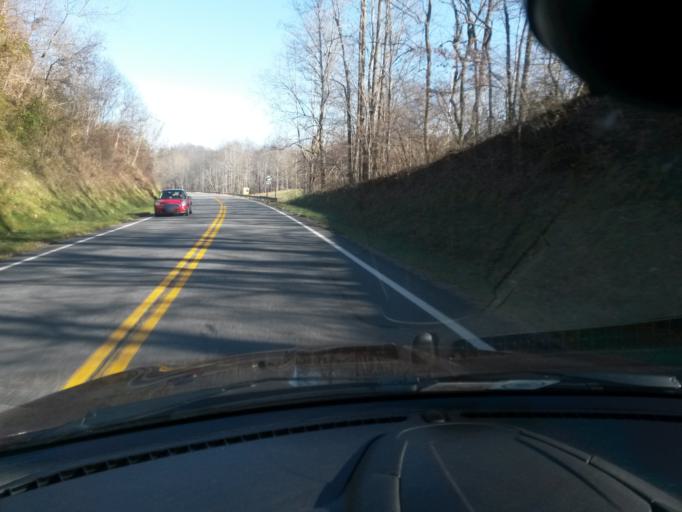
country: US
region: Virginia
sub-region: Patrick County
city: Patrick Springs
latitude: 36.7244
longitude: -80.2273
